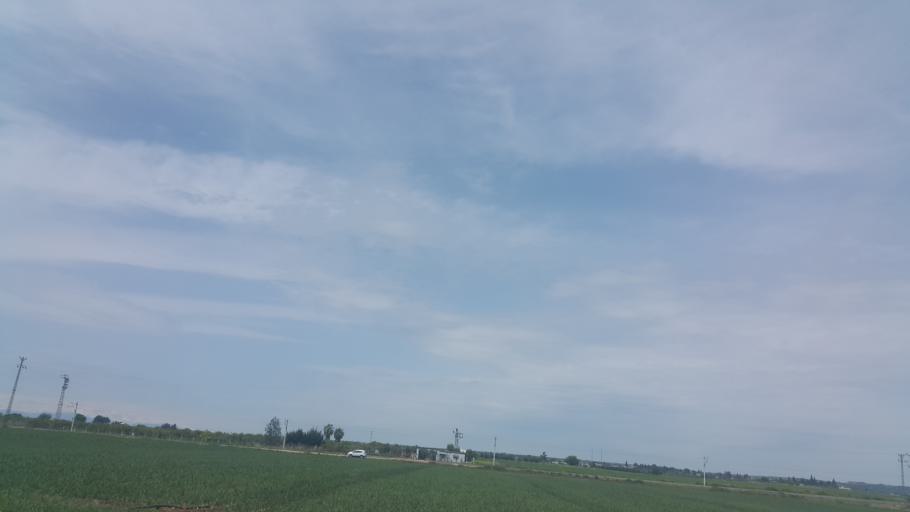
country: TR
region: Adana
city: Yakapinar
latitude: 36.9742
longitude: 35.4985
